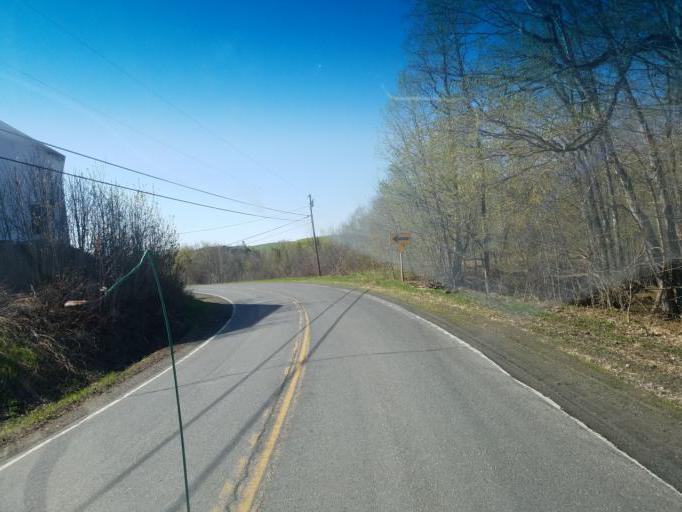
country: US
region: Maine
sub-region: Aroostook County
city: Caribou
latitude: 46.8580
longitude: -68.2084
